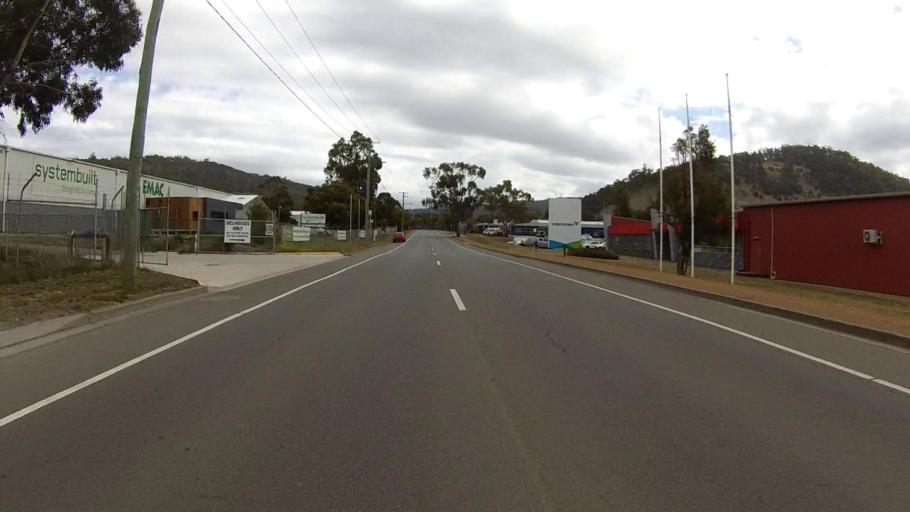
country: AU
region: Tasmania
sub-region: Clarence
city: Cambridge
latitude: -42.8346
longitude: 147.4509
